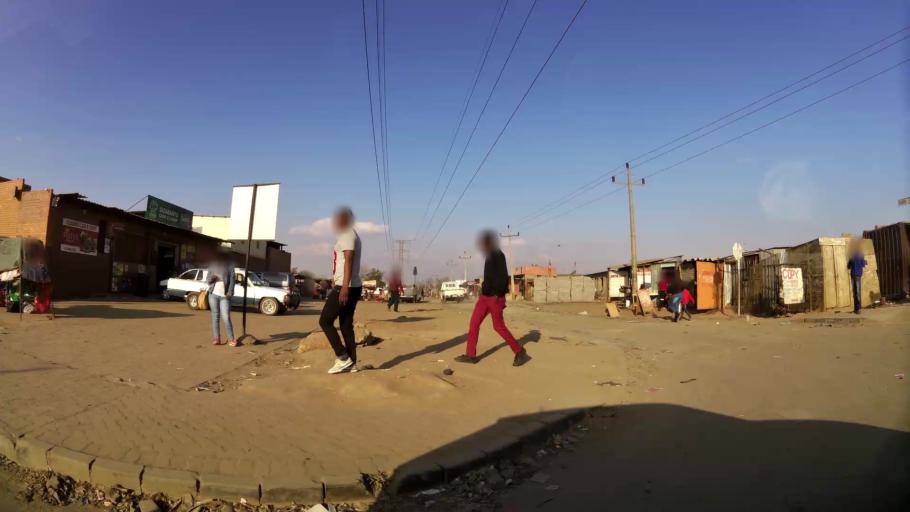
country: ZA
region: Gauteng
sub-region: Ekurhuleni Metropolitan Municipality
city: Tembisa
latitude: -25.9867
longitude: 28.2026
